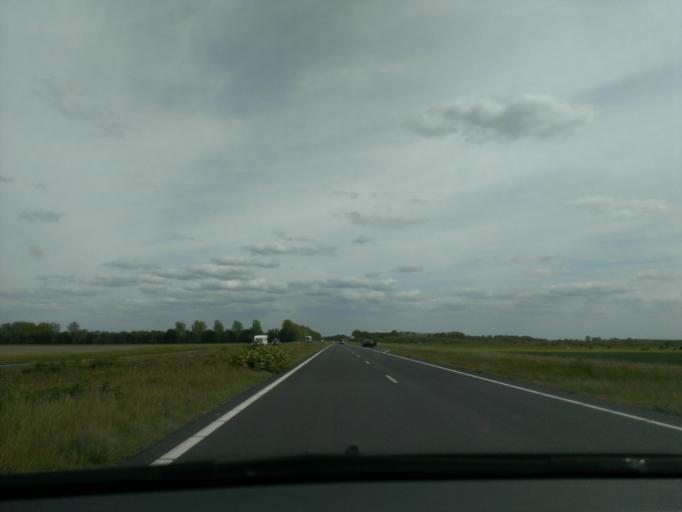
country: NL
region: Gelderland
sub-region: Gemeente Harderwijk
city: Harderwijk
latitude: 52.3825
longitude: 5.5869
